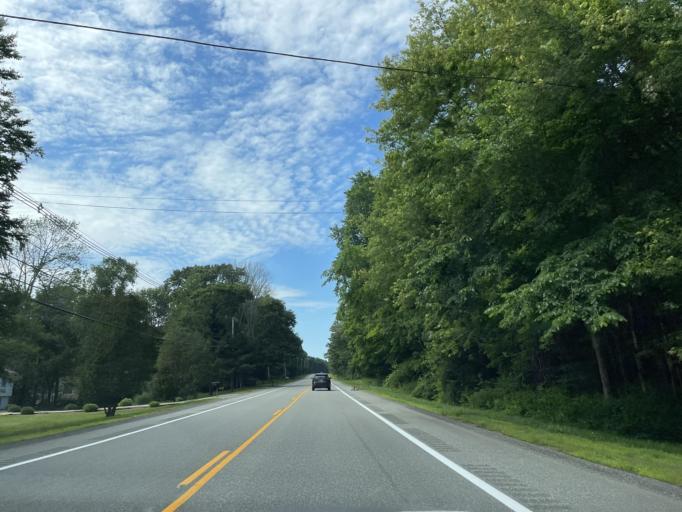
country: US
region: Rhode Island
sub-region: Kent County
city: West Greenwich
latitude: 41.6511
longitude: -71.6934
